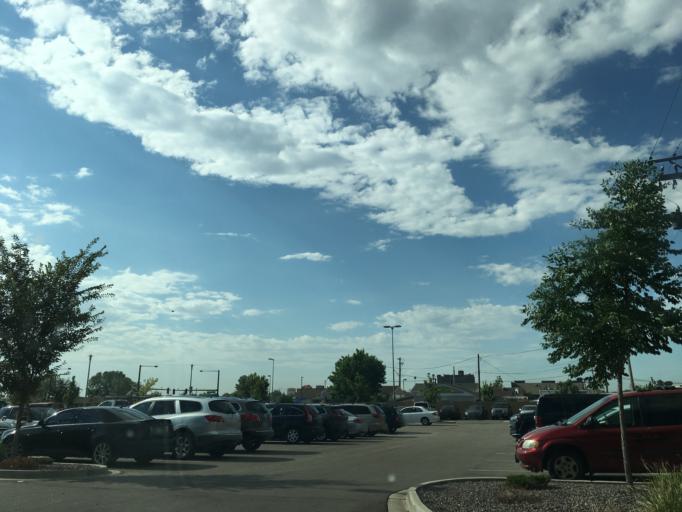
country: US
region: Colorado
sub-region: Arapahoe County
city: Sheridan
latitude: 39.6924
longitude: -105.0262
